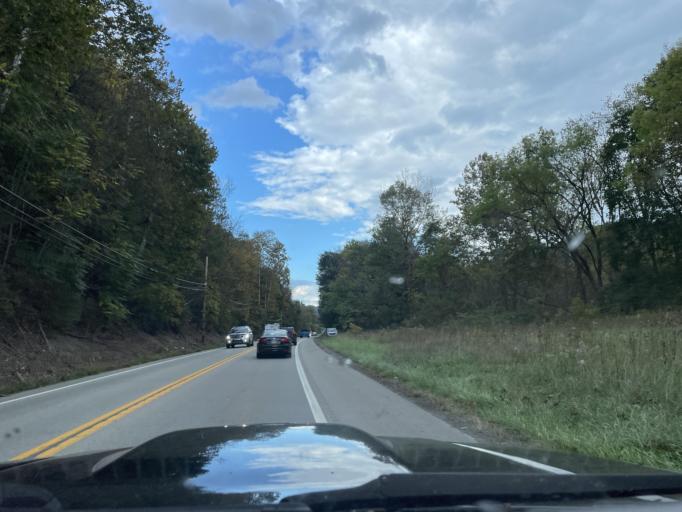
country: US
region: Pennsylvania
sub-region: Westmoreland County
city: Lower Burrell
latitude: 40.5520
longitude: -79.7500
